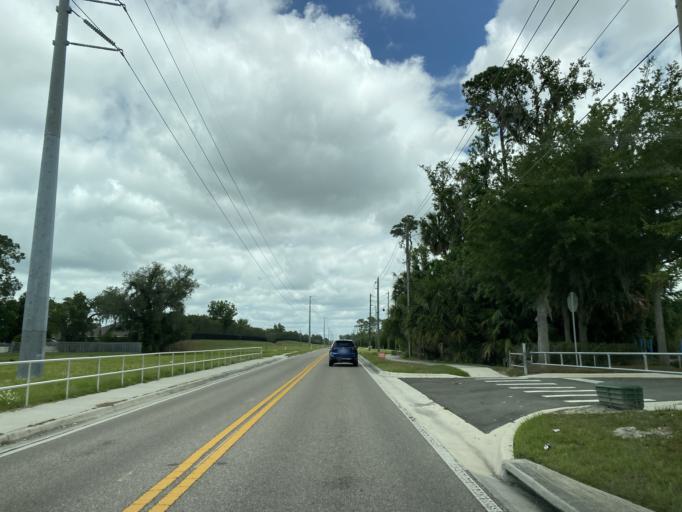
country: US
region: Florida
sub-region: Seminole County
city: Lake Mary
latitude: 28.8167
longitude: -81.3392
